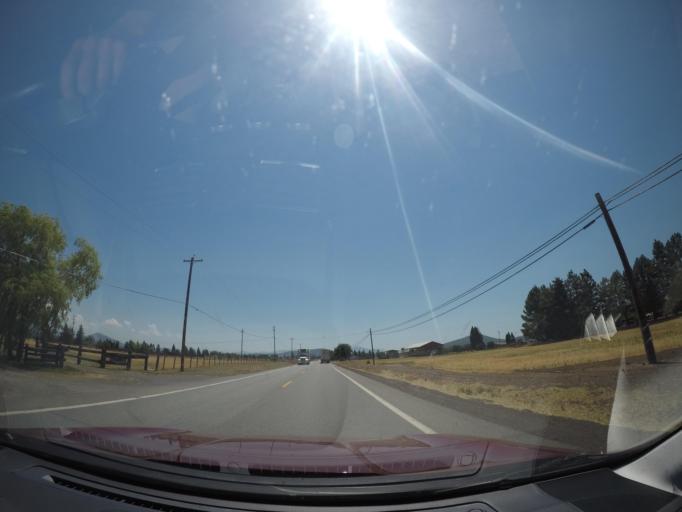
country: US
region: California
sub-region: Shasta County
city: Burney
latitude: 41.0357
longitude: -121.4154
